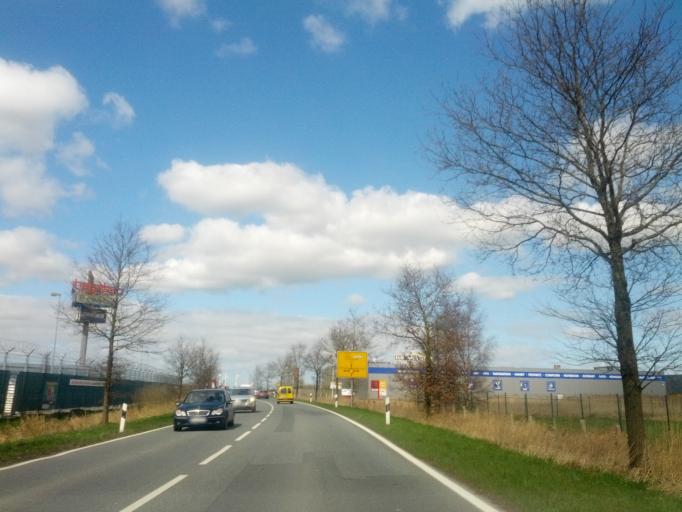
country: DE
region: Lower Saxony
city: Wittmund
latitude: 53.5824
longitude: 7.7993
